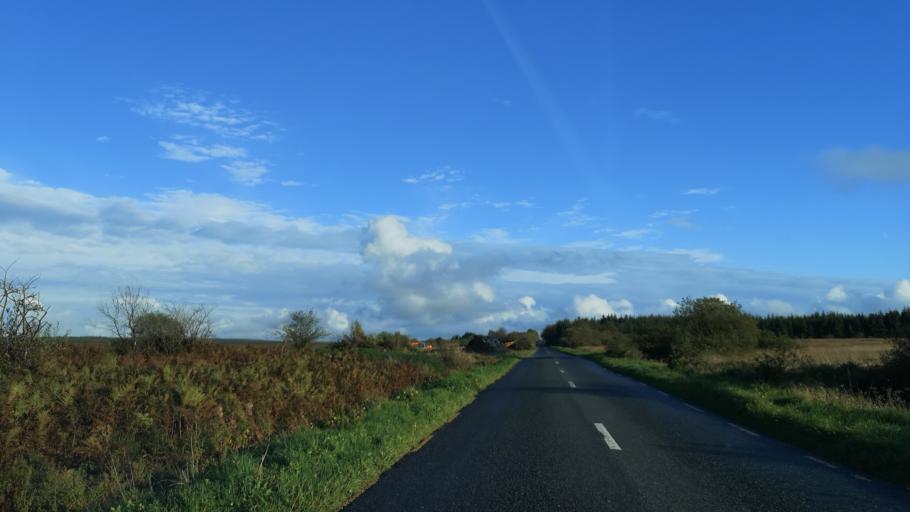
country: IE
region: Connaught
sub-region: Roscommon
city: Castlerea
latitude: 53.8148
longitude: -8.5330
